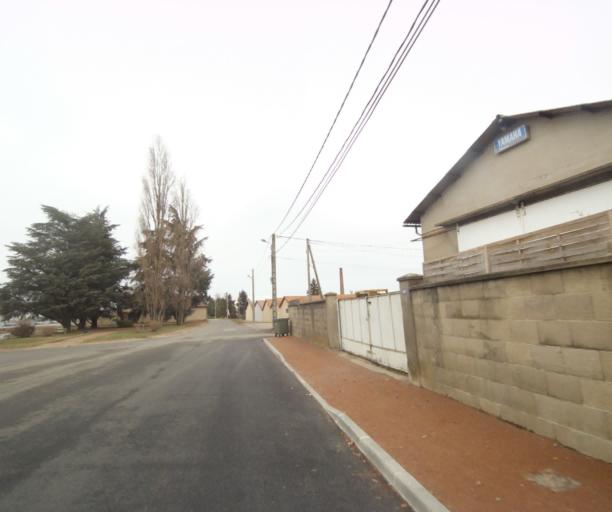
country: FR
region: Rhone-Alpes
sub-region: Departement de la Loire
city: Le Coteau
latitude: 46.0361
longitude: 4.0859
